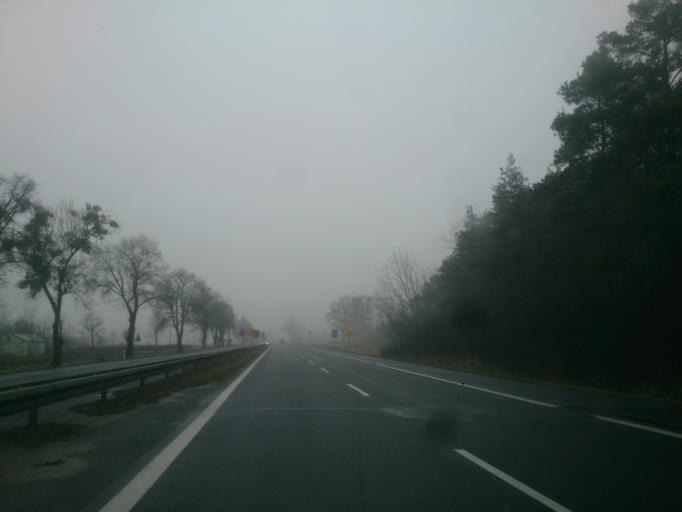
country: PL
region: Masovian Voivodeship
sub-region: Powiat nowodworski
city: Zakroczym
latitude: 52.4586
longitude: 20.5781
